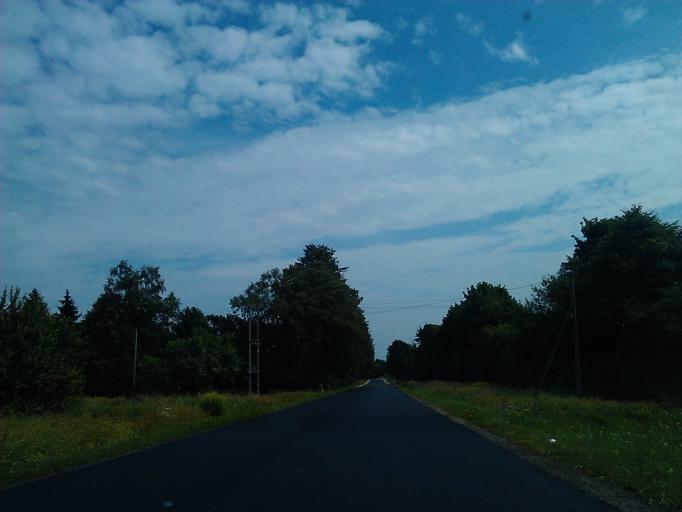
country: LV
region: Cesu Rajons
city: Cesis
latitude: 57.3270
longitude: 25.3070
